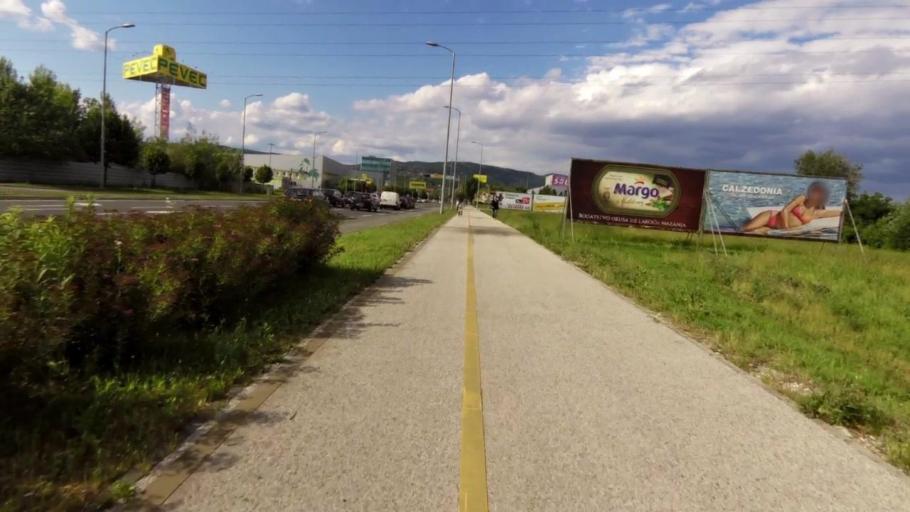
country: HR
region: Grad Zagreb
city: Jezdovec
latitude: 45.8006
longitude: 15.8574
